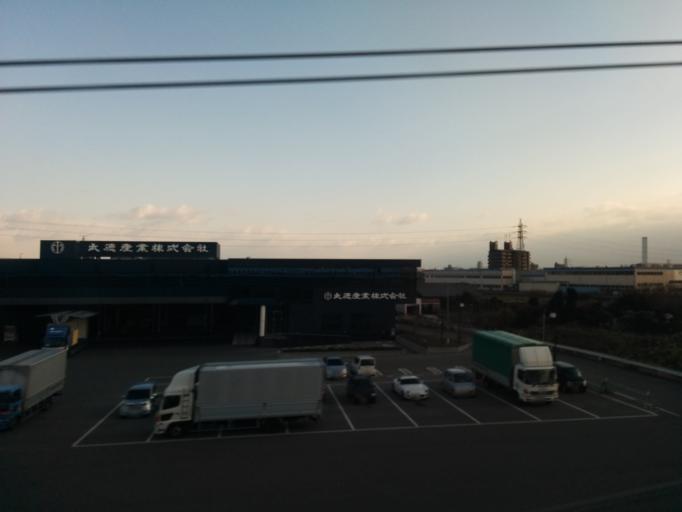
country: JP
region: Aichi
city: Inazawa
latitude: 35.2354
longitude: 136.7891
